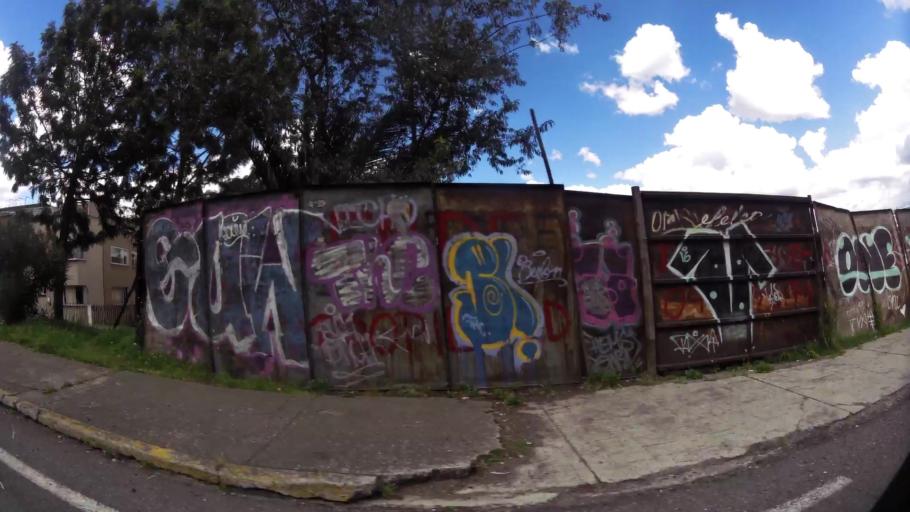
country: EC
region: Pichincha
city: Quito
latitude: -0.2045
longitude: -78.5106
